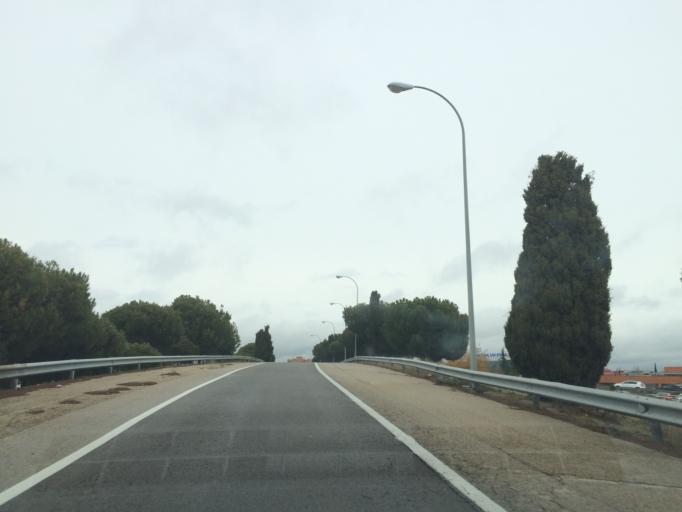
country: ES
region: Madrid
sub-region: Provincia de Madrid
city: Tres Cantos
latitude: 40.6009
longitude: -3.7196
